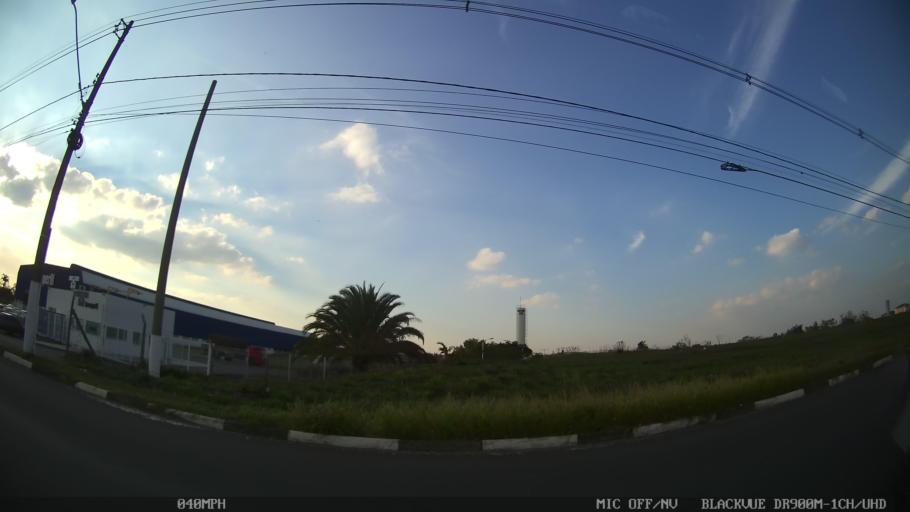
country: BR
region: Sao Paulo
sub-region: Hortolandia
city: Hortolandia
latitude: -22.8758
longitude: -47.1773
